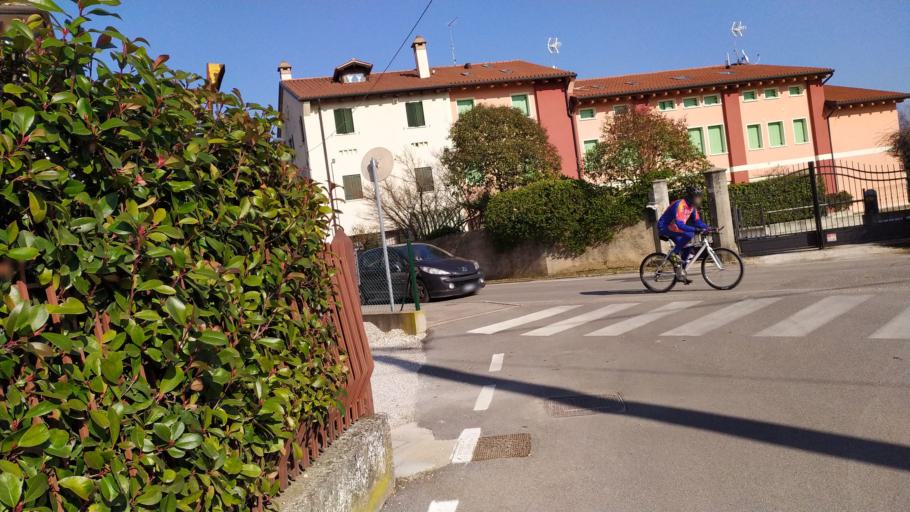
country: IT
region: Veneto
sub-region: Provincia di Treviso
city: Volpago del Montello
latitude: 45.7799
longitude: 12.1210
